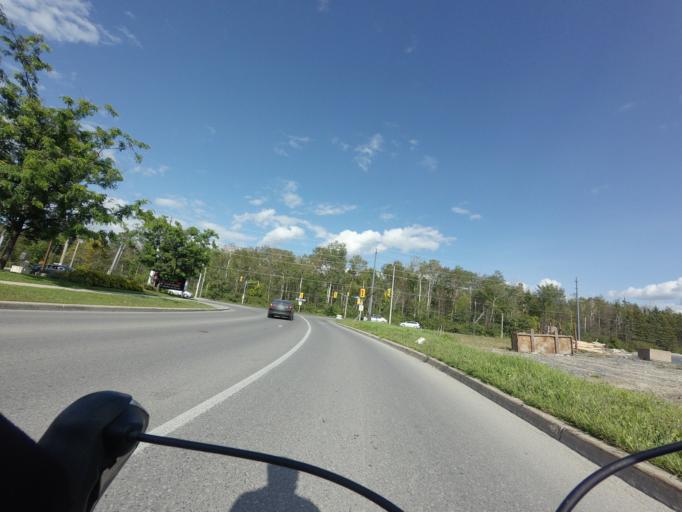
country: CA
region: Ontario
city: Bells Corners
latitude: 45.2808
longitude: -75.8380
